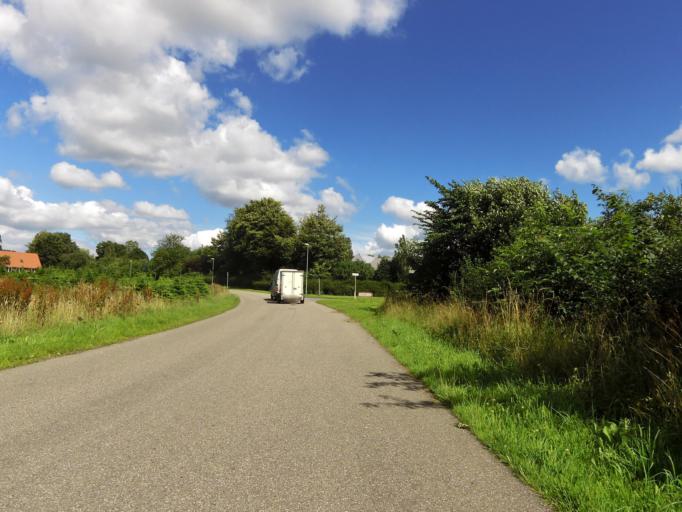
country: DK
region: South Denmark
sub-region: Haderslev Kommune
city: Gram
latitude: 55.3032
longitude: 9.1443
